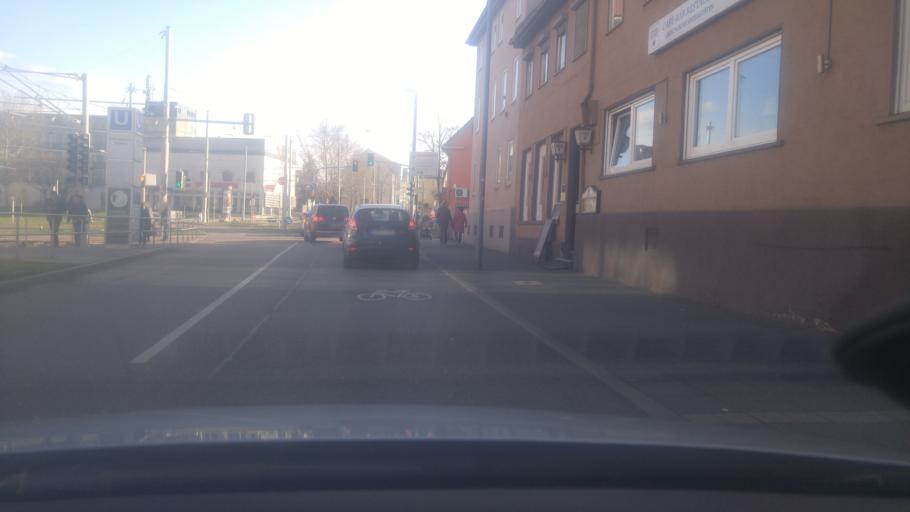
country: DE
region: Baden-Wuerttemberg
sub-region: Regierungsbezirk Stuttgart
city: Stuttgart Feuerbach
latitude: 48.8303
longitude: 9.1745
